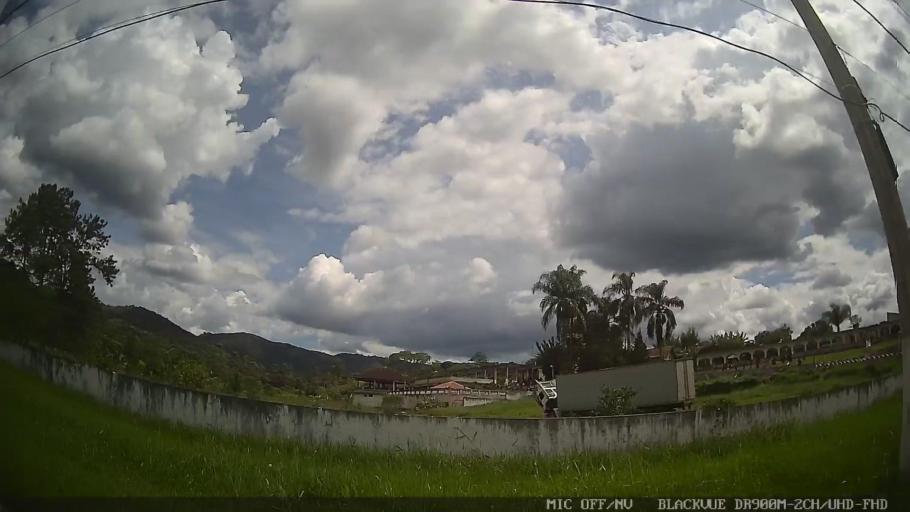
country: BR
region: Sao Paulo
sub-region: Rio Grande Da Serra
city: Rio Grande da Serra
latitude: -23.6964
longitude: -46.2382
